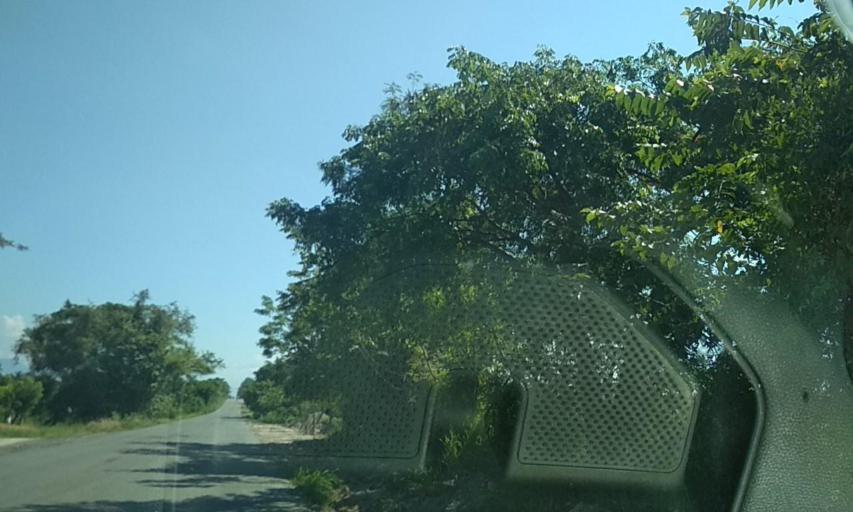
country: MX
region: Veracruz
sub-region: Martinez de la Torre
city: La Union Paso Largo
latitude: 20.1474
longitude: -97.0001
